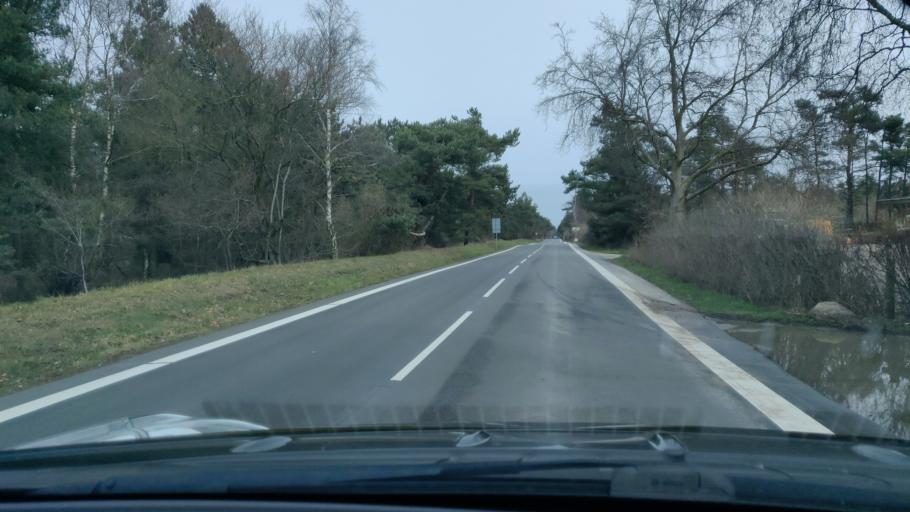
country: DK
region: Zealand
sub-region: Odsherred Kommune
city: Hojby
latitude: 55.8860
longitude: 11.5521
